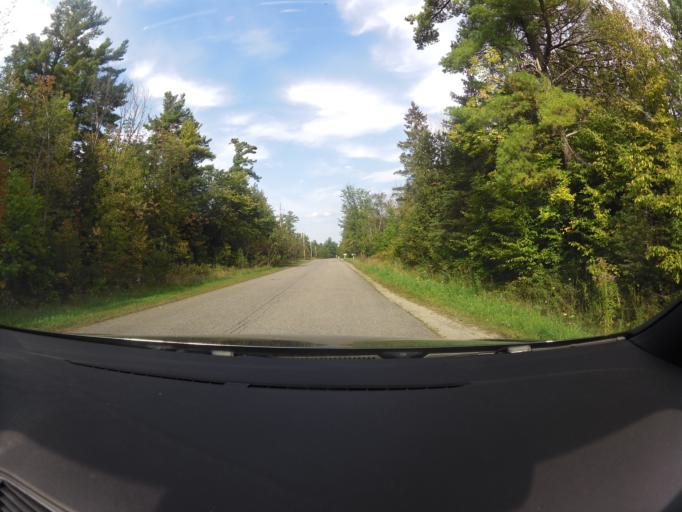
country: CA
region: Ontario
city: Carleton Place
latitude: 45.3459
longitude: -76.1452
